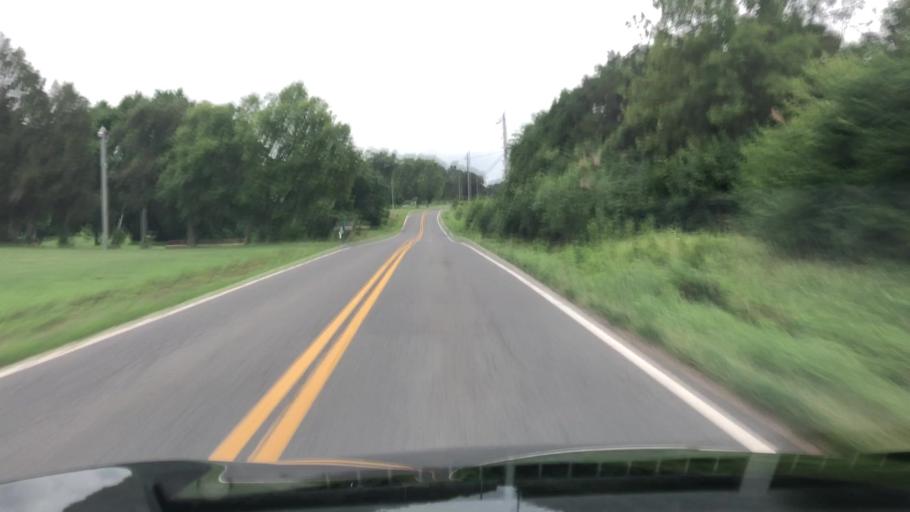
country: US
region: Virginia
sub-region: Prince William County
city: Nokesville
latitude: 38.5892
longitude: -77.6048
